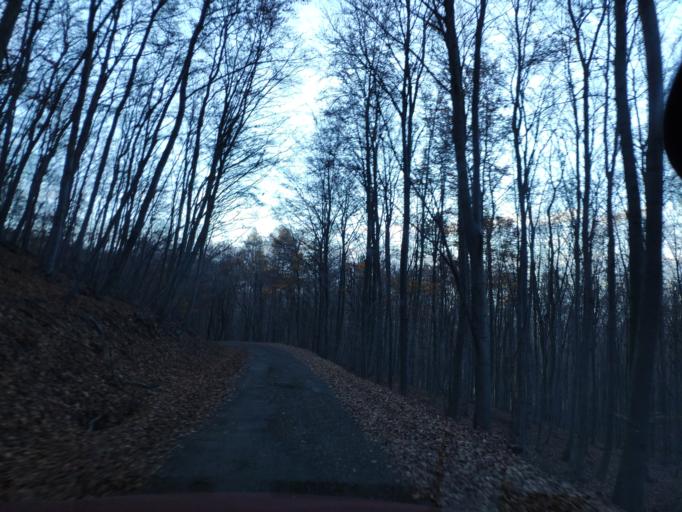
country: SK
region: Kosicky
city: Secovce
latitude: 48.5839
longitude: 21.5075
